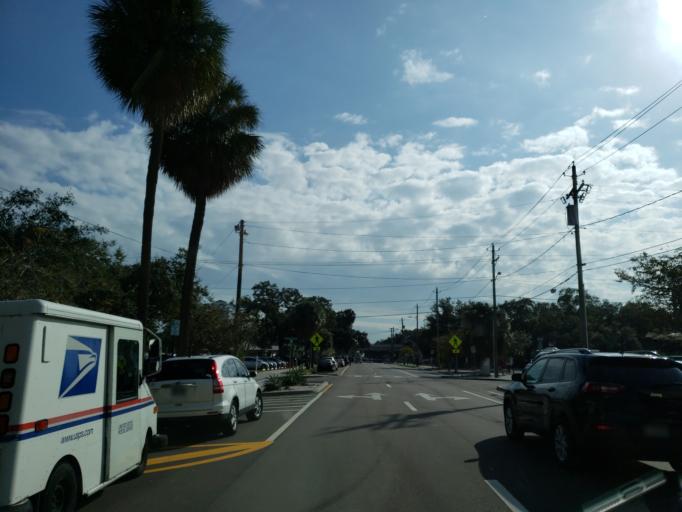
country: US
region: Florida
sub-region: Hillsborough County
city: Tampa
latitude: 27.9450
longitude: -82.4638
